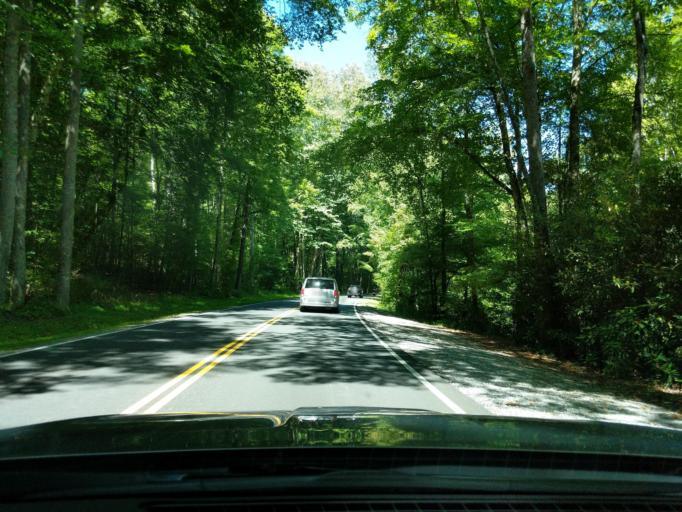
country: US
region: North Carolina
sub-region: Swain County
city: Cherokee
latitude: 35.5358
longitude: -83.3034
